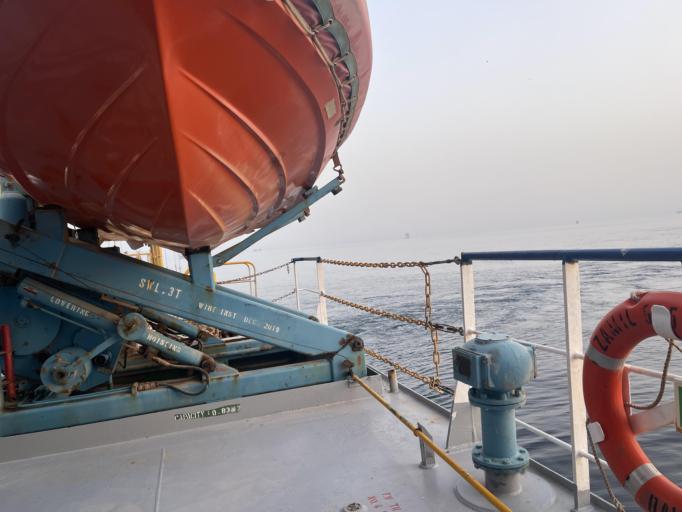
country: SA
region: Eastern Province
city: As Saffaniyah
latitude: 28.3891
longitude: 49.2588
